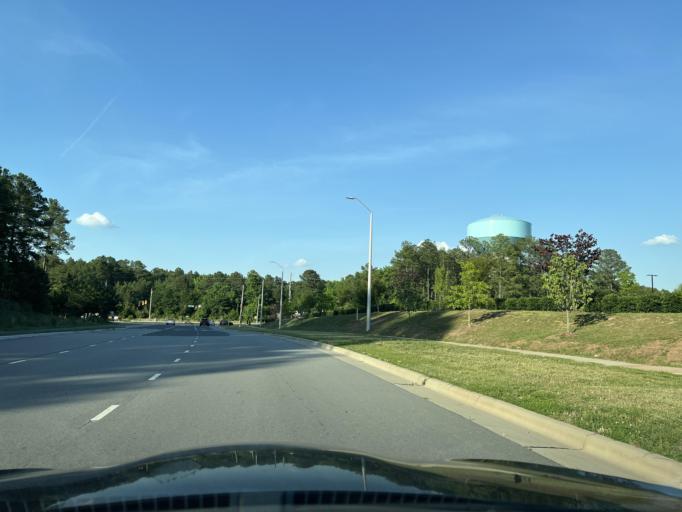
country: US
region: North Carolina
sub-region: Wake County
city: Green Level
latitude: 35.8297
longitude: -78.8794
